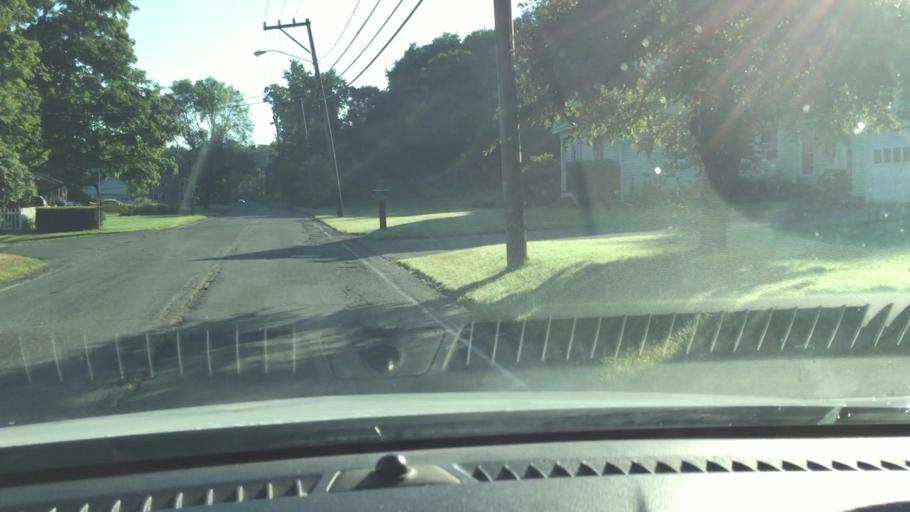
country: US
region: Massachusetts
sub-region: Berkshire County
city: Pittsfield
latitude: 42.4161
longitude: -73.2283
